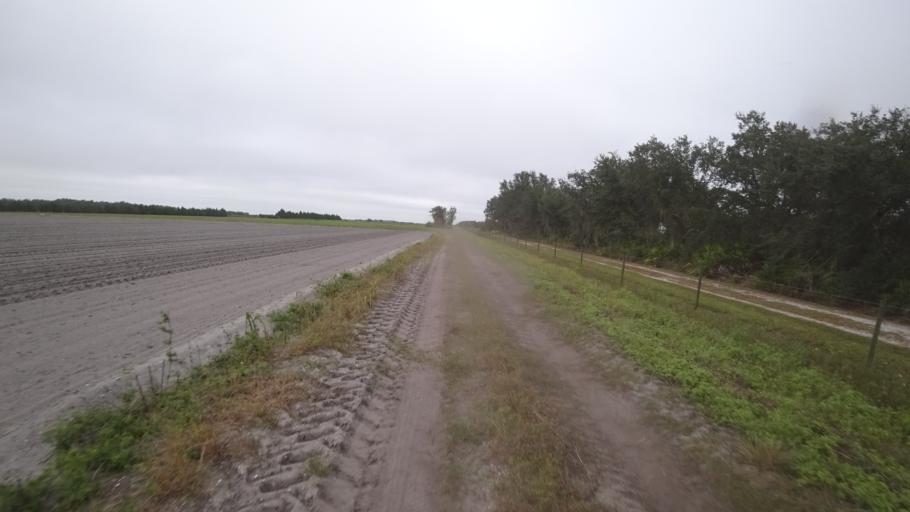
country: US
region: Florida
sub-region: Sarasota County
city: Warm Mineral Springs
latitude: 27.2798
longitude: -82.1346
